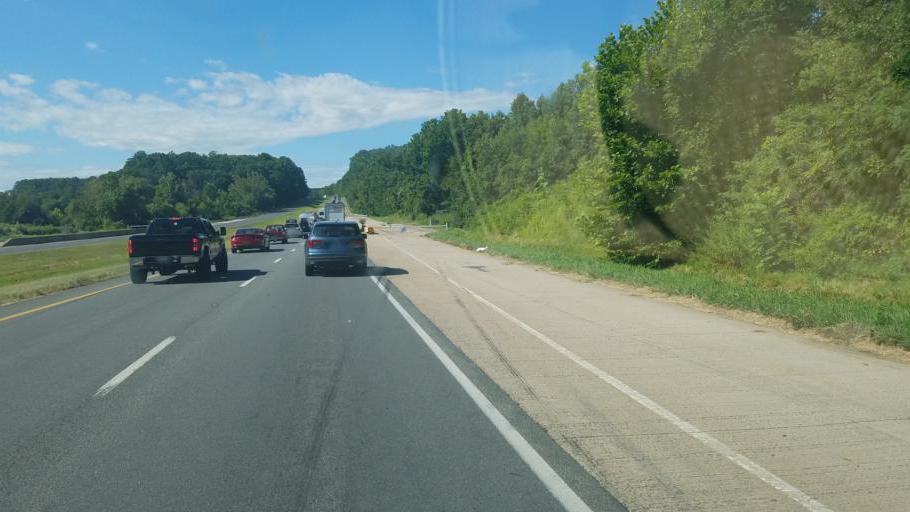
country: US
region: Virginia
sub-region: Fauquier County
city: Warrenton
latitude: 38.6962
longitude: -77.7818
